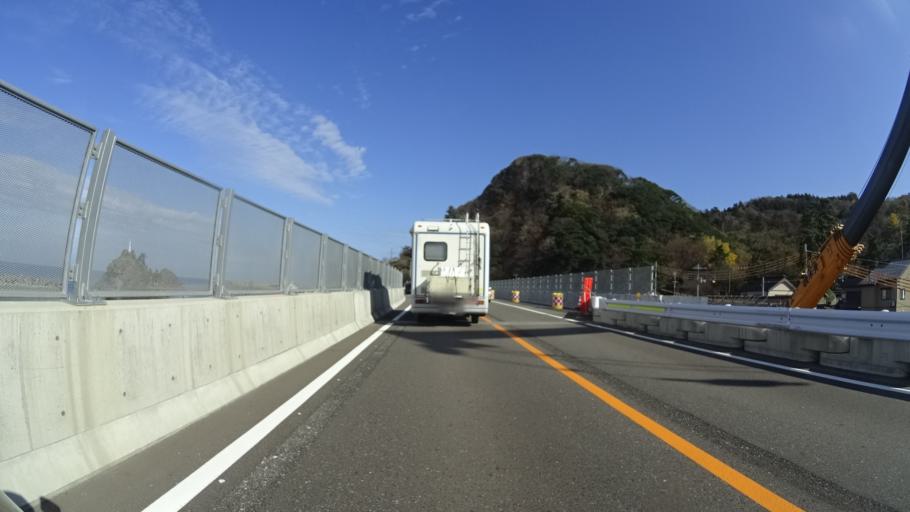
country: JP
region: Niigata
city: Itoigawa
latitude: 37.1068
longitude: 137.9923
